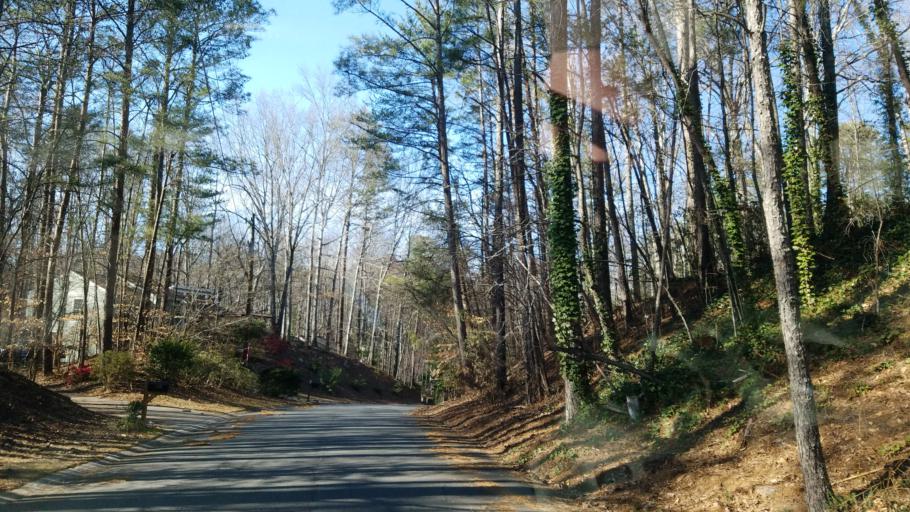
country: US
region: Georgia
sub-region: Fulton County
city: Roswell
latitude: 34.0385
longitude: -84.4361
